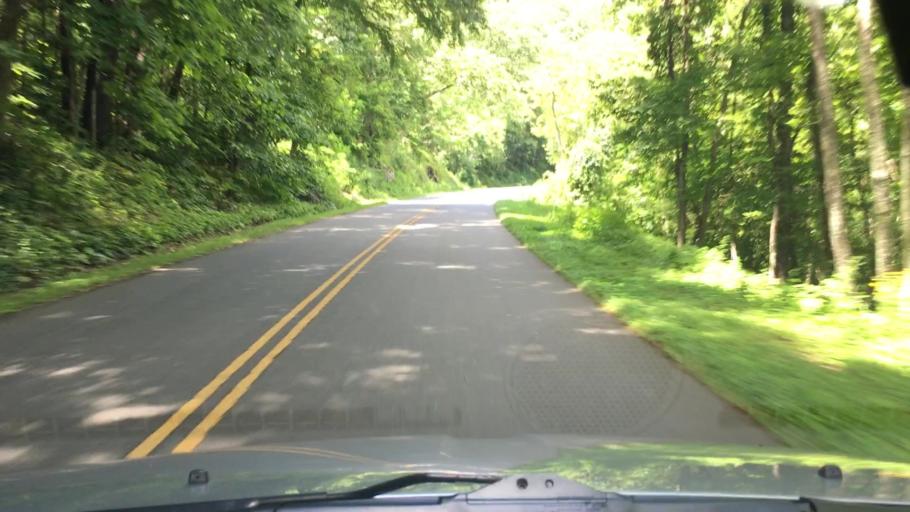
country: US
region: North Carolina
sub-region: Buncombe County
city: Swannanoa
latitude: 35.6595
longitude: -82.4497
